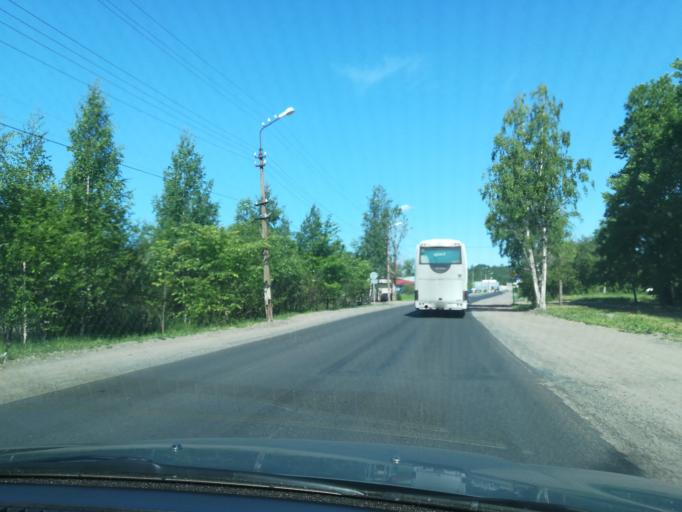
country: RU
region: Leningrad
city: Svetogorsk
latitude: 61.1156
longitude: 28.8520
